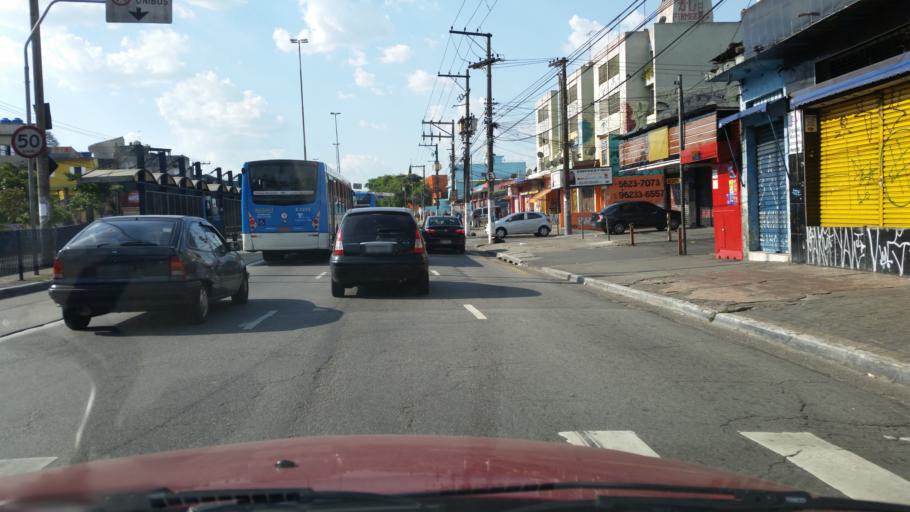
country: BR
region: Sao Paulo
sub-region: Diadema
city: Diadema
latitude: -23.6755
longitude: -46.6422
